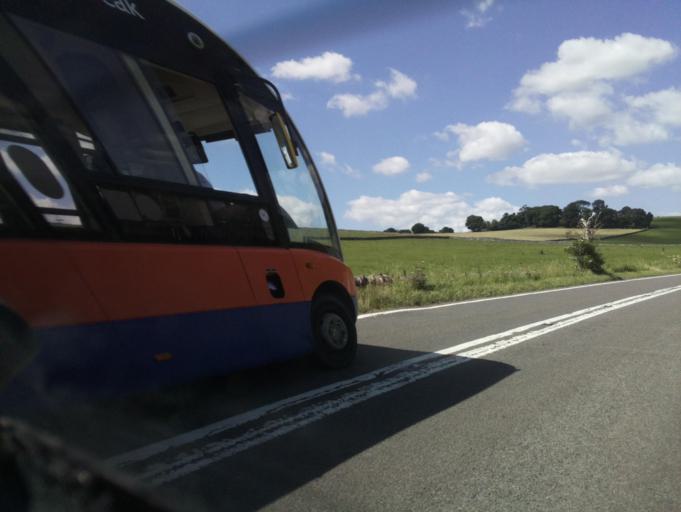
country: GB
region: England
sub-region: Derbyshire
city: Ashbourne
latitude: 53.0747
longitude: -1.7564
